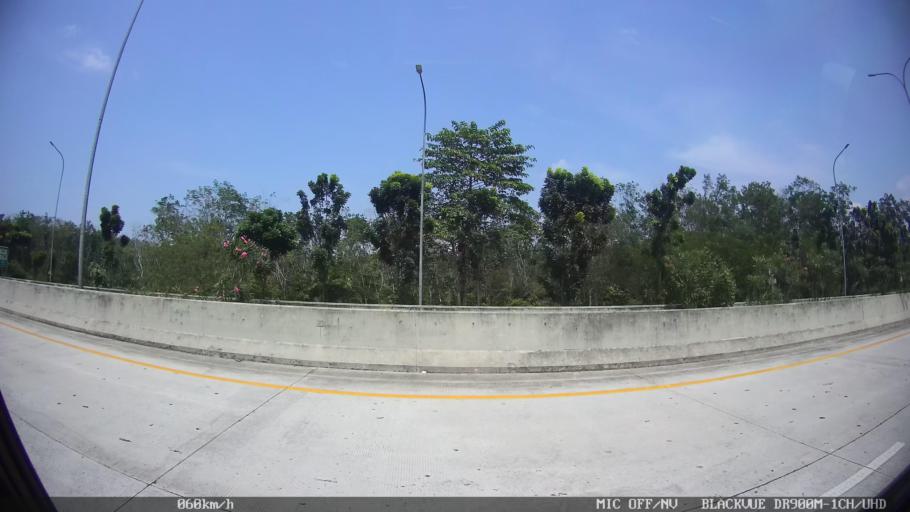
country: ID
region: Lampung
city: Kedaton
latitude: -5.3610
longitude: 105.3252
